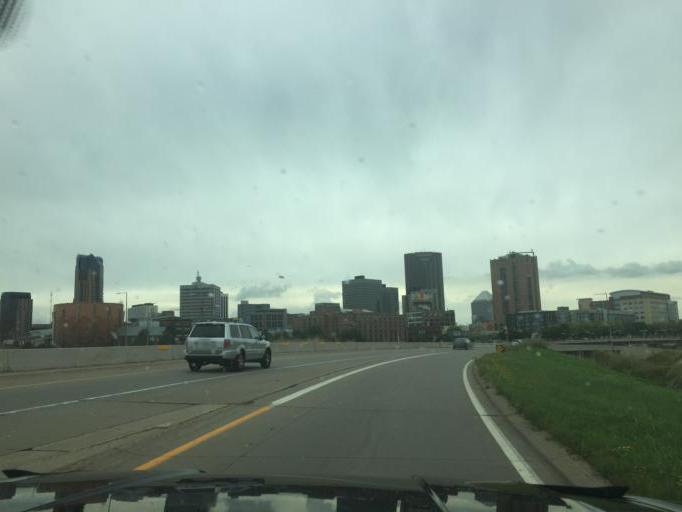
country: US
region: Minnesota
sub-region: Ramsey County
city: Saint Paul
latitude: 44.9558
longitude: -93.0921
